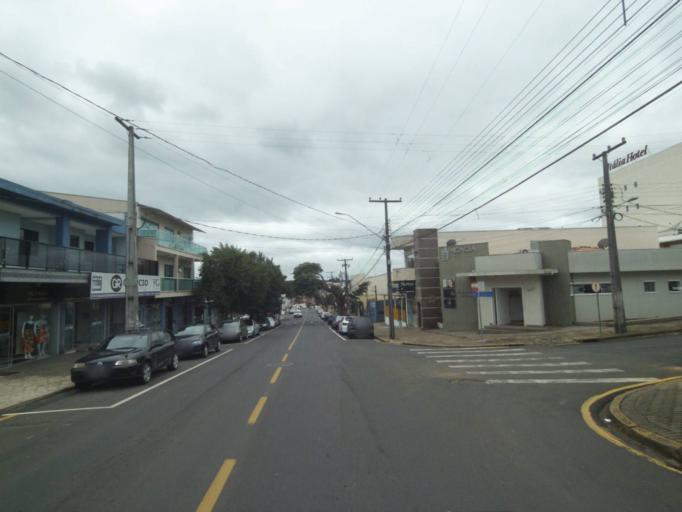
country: BR
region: Parana
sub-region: Telemaco Borba
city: Telemaco Borba
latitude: -24.3258
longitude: -50.6212
